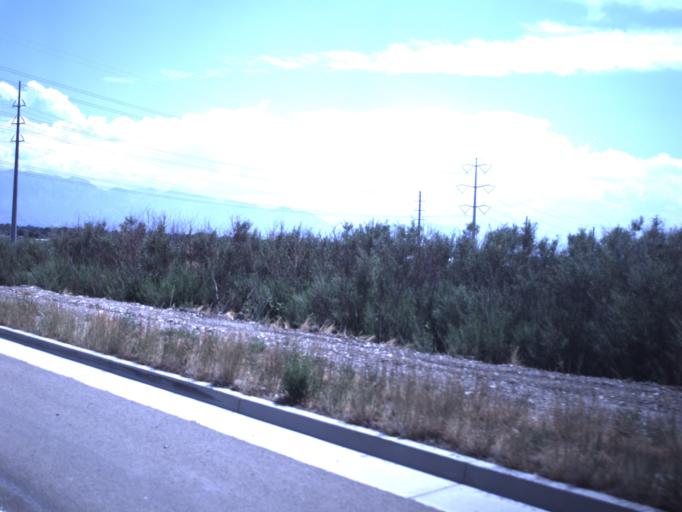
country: US
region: Utah
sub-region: Utah County
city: Lehi
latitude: 40.4125
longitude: -111.9104
